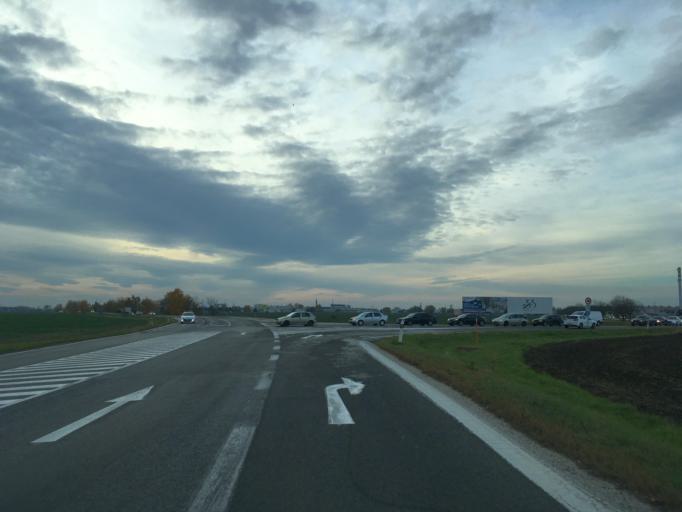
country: SK
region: Trnavsky
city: Dunajska Streda
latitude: 47.9818
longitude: 17.6476
